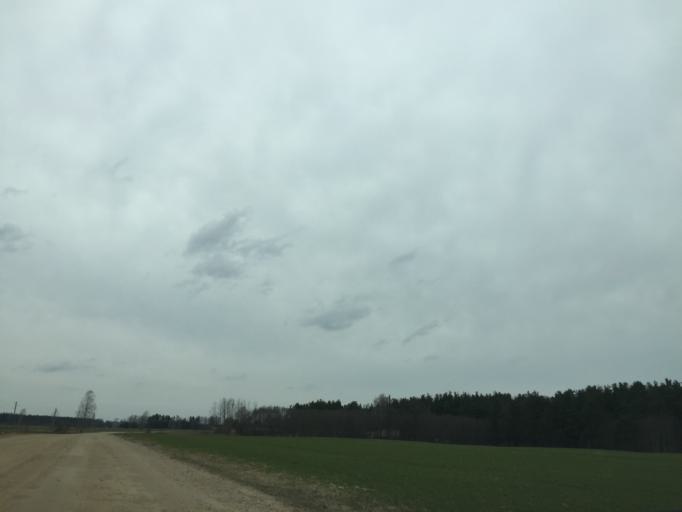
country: LV
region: Livani
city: Livani
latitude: 56.3117
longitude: 26.1622
